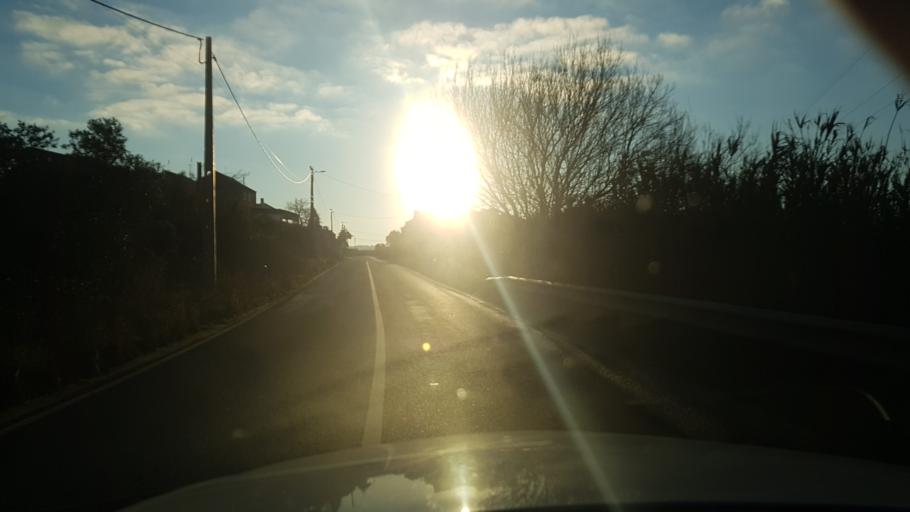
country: PT
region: Santarem
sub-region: Torres Novas
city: Torres Novas
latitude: 39.5555
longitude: -8.5699
